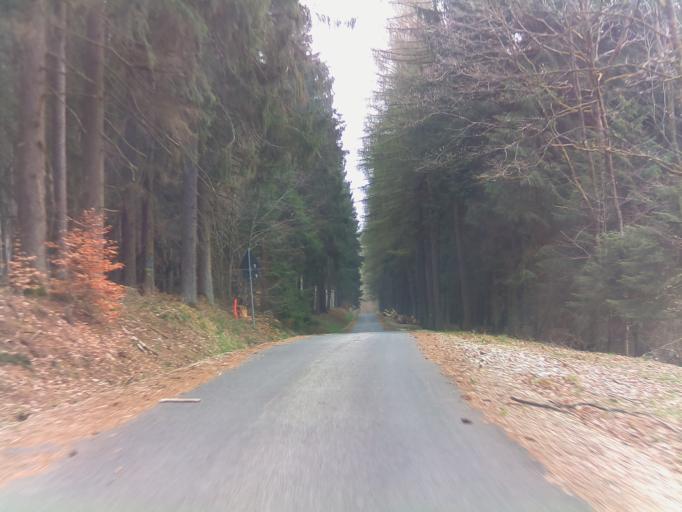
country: DE
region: Rheinland-Pfalz
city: Schwollen
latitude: 49.7206
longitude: 7.1732
